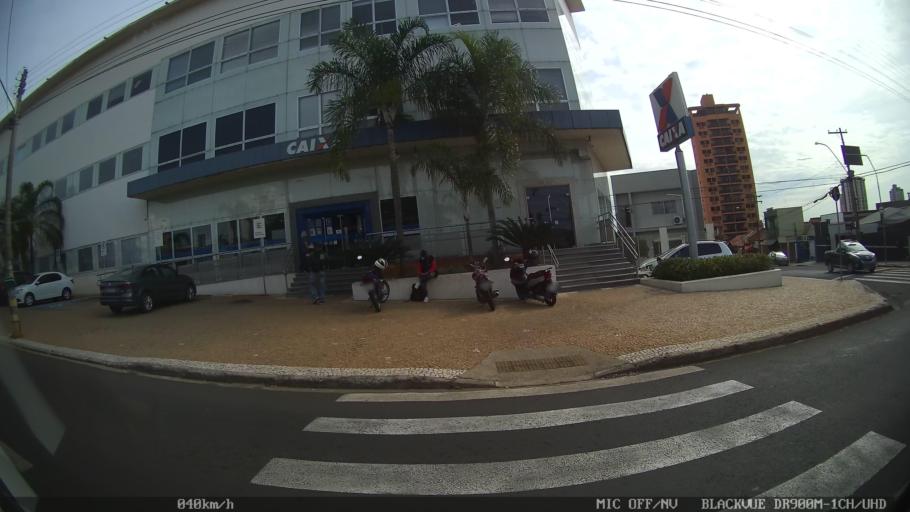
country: BR
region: Sao Paulo
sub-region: Piracicaba
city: Piracicaba
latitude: -22.7188
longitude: -47.6330
